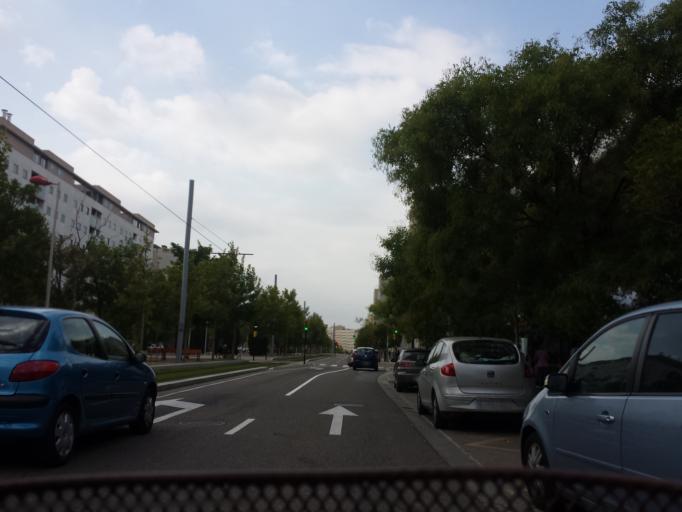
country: ES
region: Aragon
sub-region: Provincia de Zaragoza
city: Montecanal
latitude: 41.6218
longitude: -0.9198
